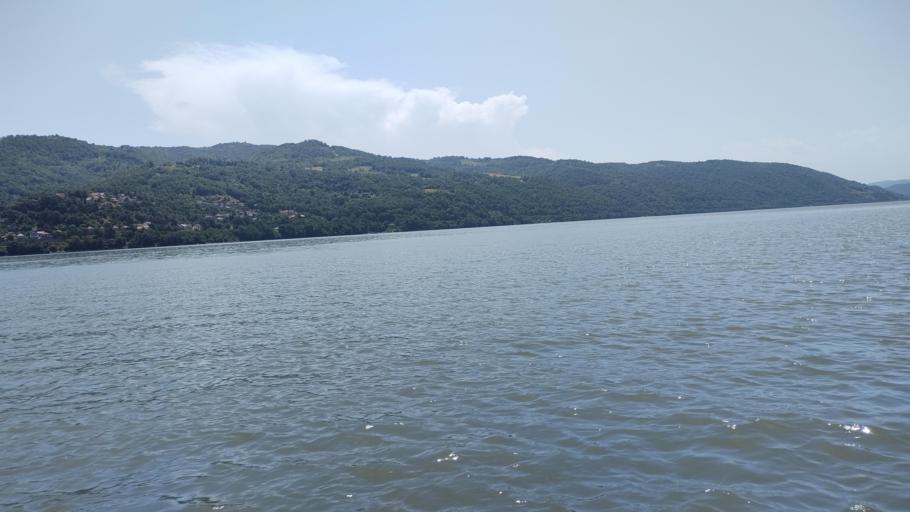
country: RO
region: Mehedinti
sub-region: Comuna Svinita
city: Svinita
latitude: 44.5038
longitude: 22.1918
